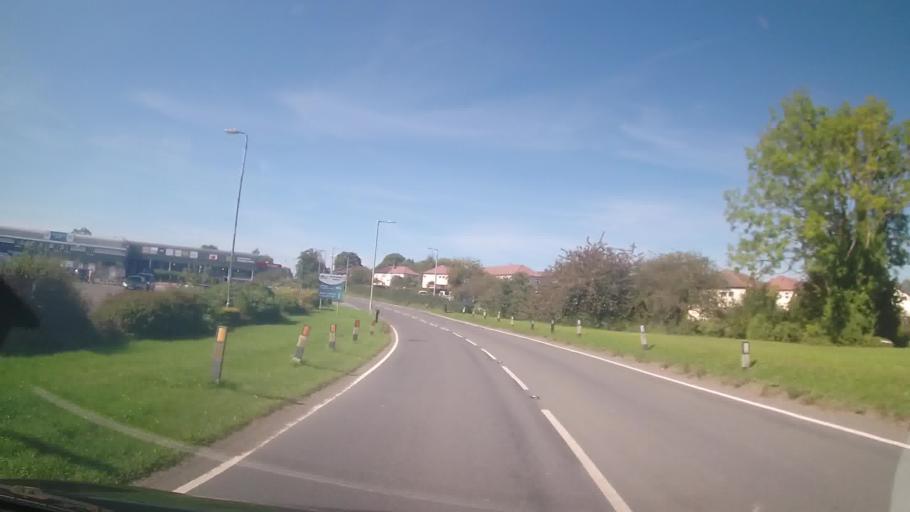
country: GB
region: England
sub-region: Shropshire
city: Mainstone
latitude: 52.5363
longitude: -3.0622
